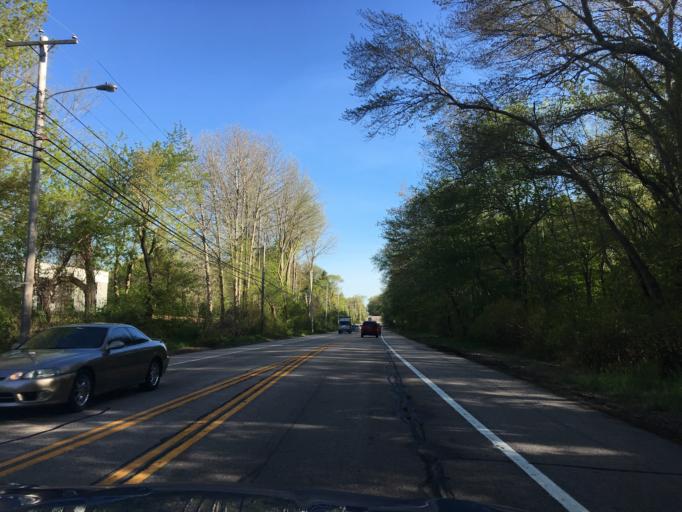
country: US
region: Rhode Island
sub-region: Kent County
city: East Greenwich
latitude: 41.6432
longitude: -71.4952
